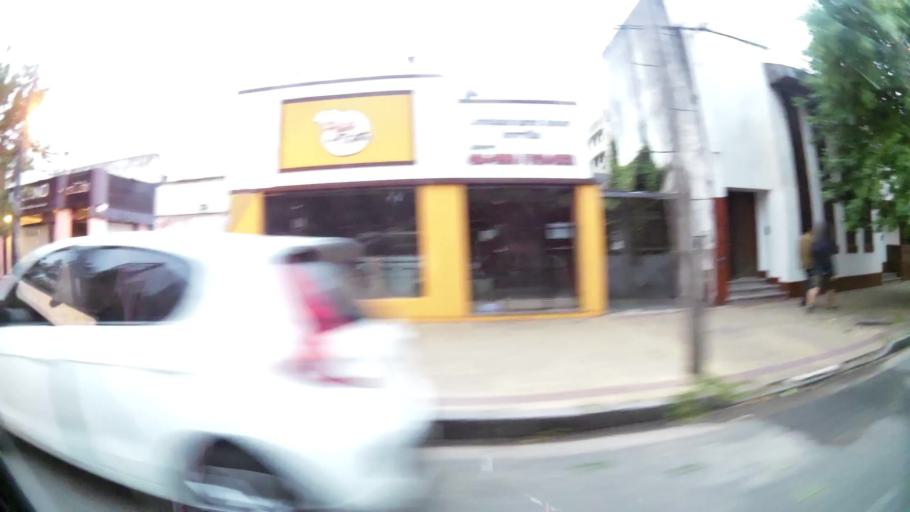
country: AR
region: Buenos Aires
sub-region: Partido de La Plata
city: La Plata
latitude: -34.9185
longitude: -57.9639
